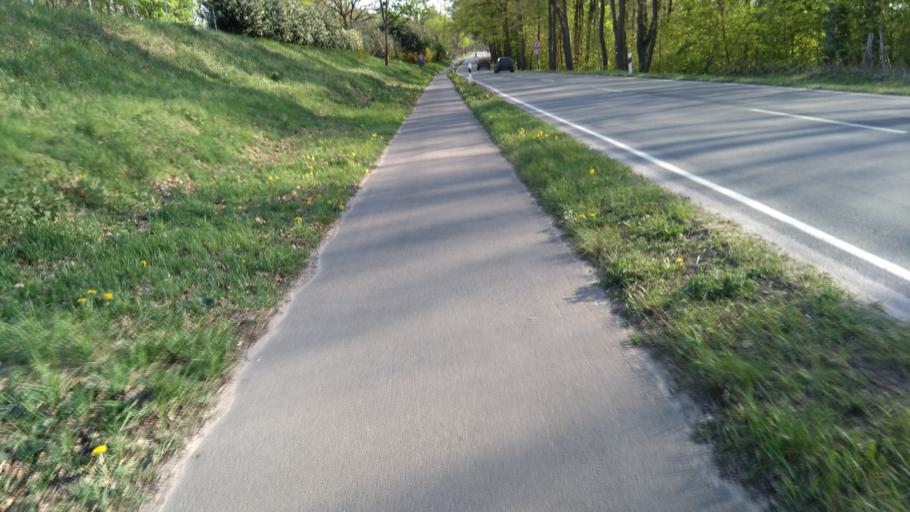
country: DE
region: Lower Saxony
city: Buxtehude
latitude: 53.4553
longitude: 9.6960
